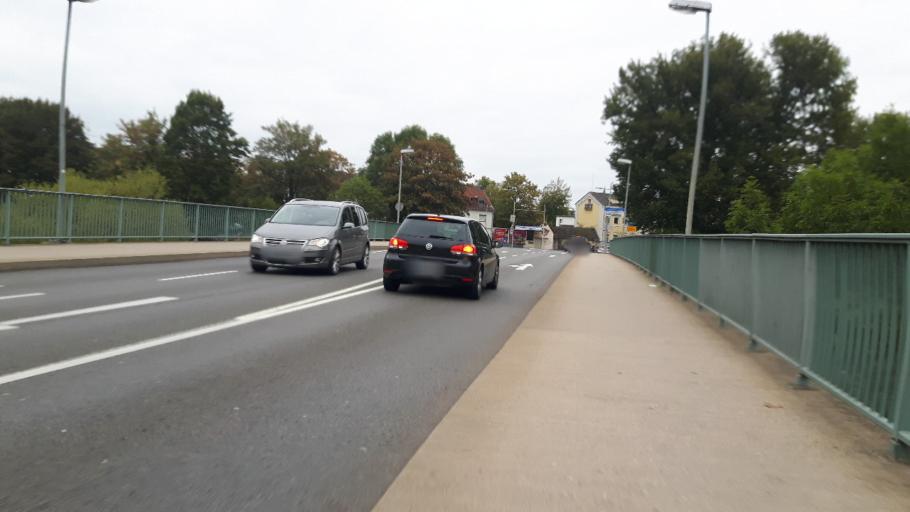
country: DE
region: North Rhine-Westphalia
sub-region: Regierungsbezirk Koln
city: Siegburg
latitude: 50.7895
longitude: 7.2008
